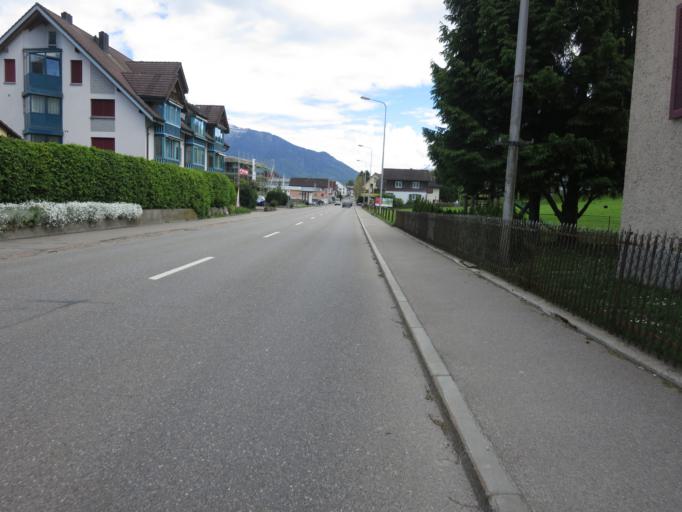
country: CH
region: Schwyz
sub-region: Bezirk March
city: Schubelbach
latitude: 47.1751
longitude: 8.9502
